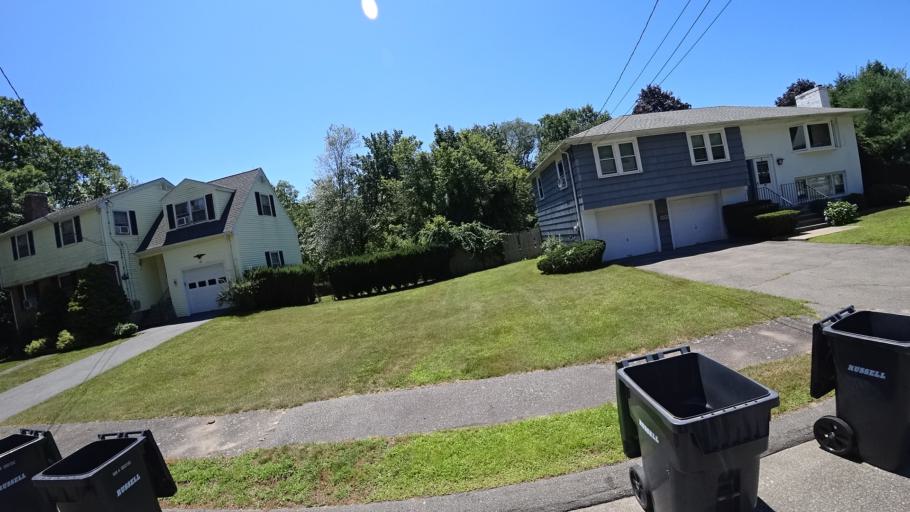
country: US
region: Massachusetts
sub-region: Norfolk County
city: Dedham
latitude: 42.2226
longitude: -71.1503
